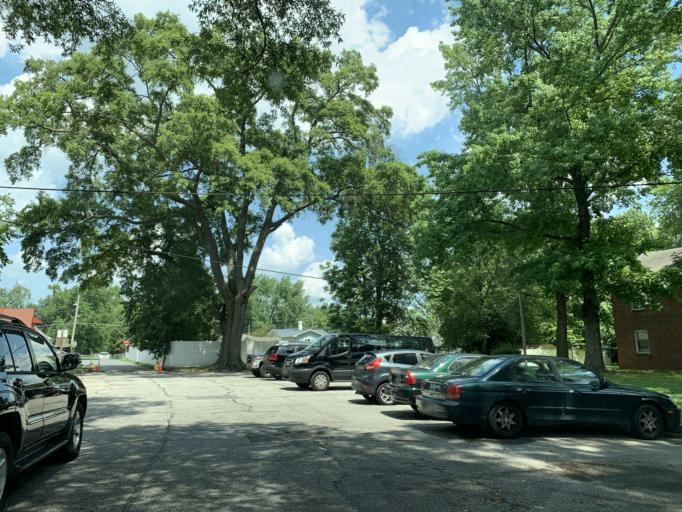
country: US
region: Maryland
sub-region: Baltimore County
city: Essex
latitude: 39.3066
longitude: -76.4661
